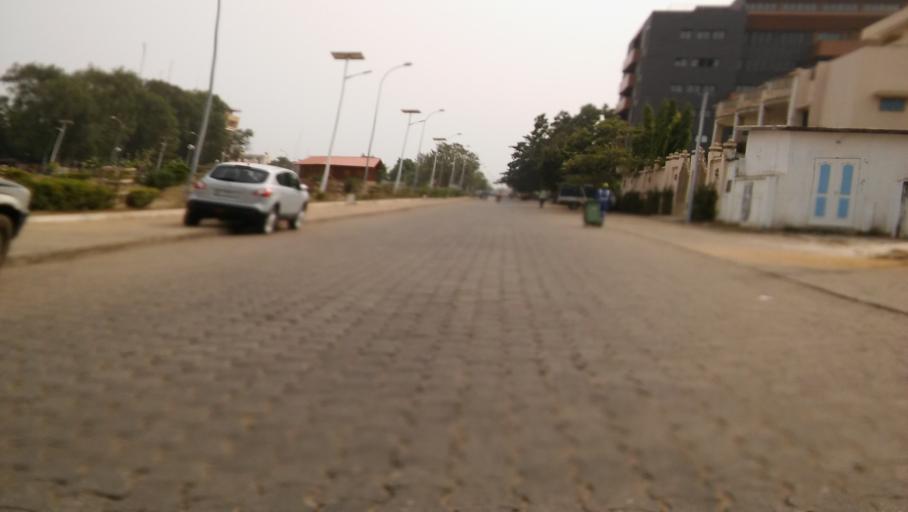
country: BJ
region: Littoral
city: Cotonou
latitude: 6.3558
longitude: 2.4072
